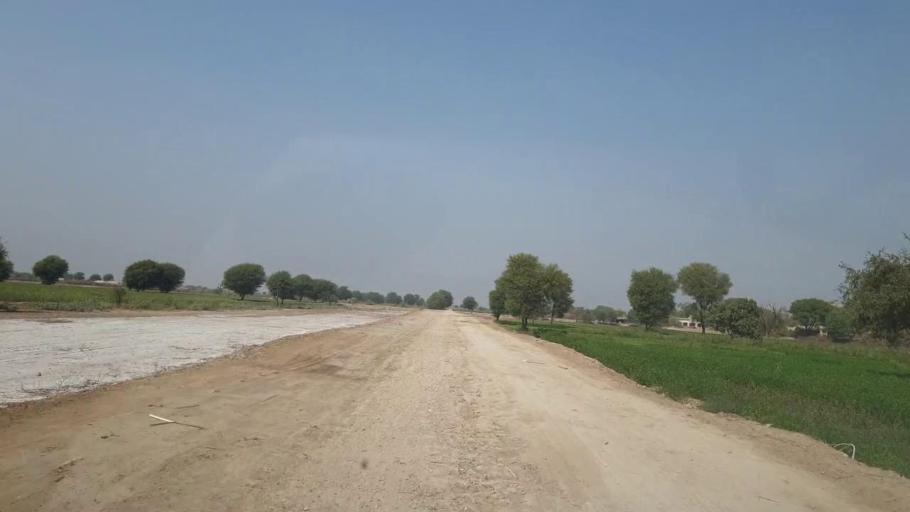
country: PK
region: Sindh
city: Mirpur Khas
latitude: 25.6564
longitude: 69.1347
